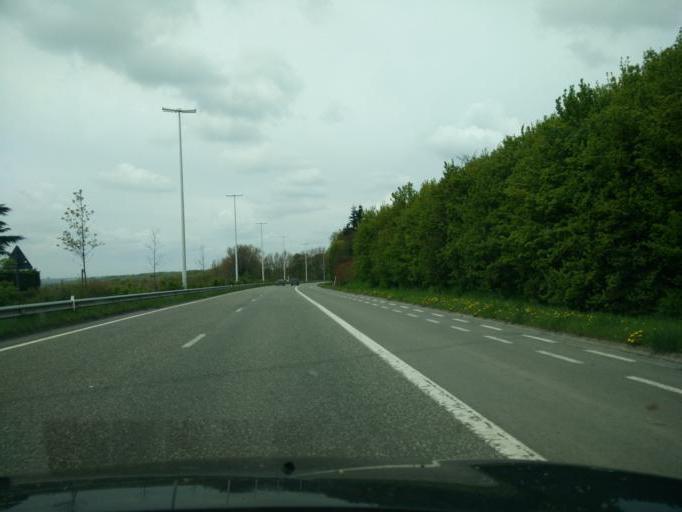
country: BE
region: Flanders
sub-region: Provincie Oost-Vlaanderen
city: Ronse
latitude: 50.7735
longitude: 3.5898
